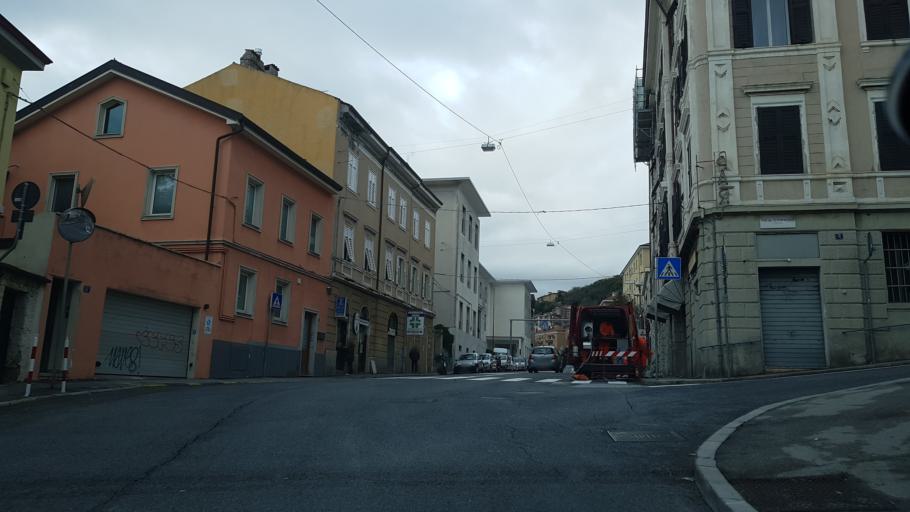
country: IT
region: Friuli Venezia Giulia
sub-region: Provincia di Trieste
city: Villa Opicina
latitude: 45.6662
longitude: 13.7664
